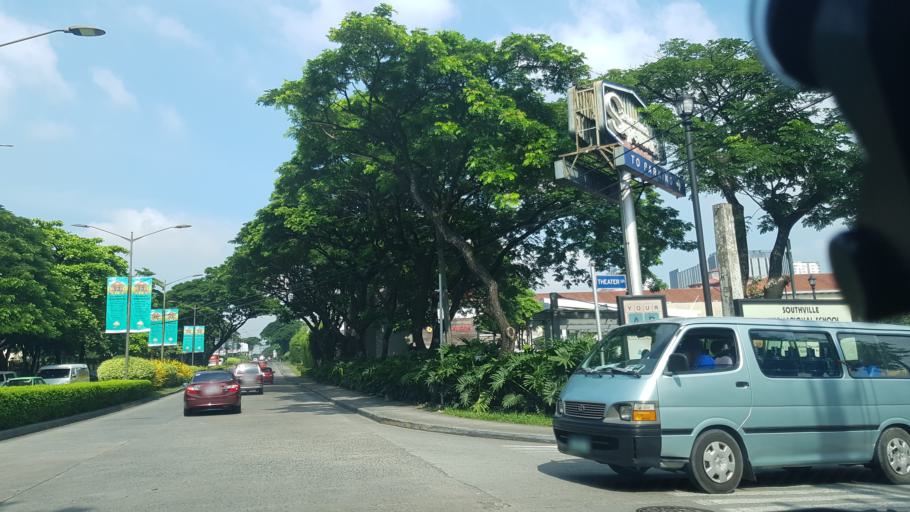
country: PH
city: Sambayanihan People's Village
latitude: 14.4217
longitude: 121.0309
